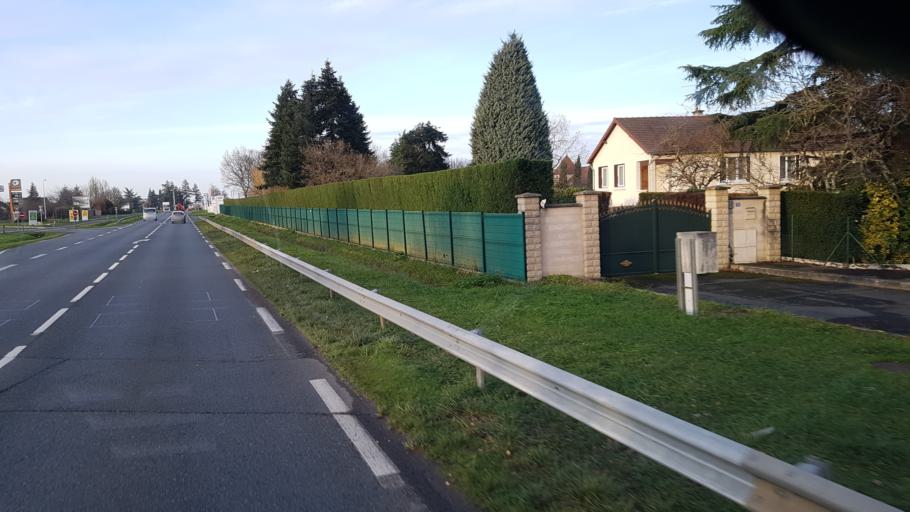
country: FR
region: Centre
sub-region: Departement de l'Indre
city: Chateauroux
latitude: 46.7937
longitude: 1.7178
